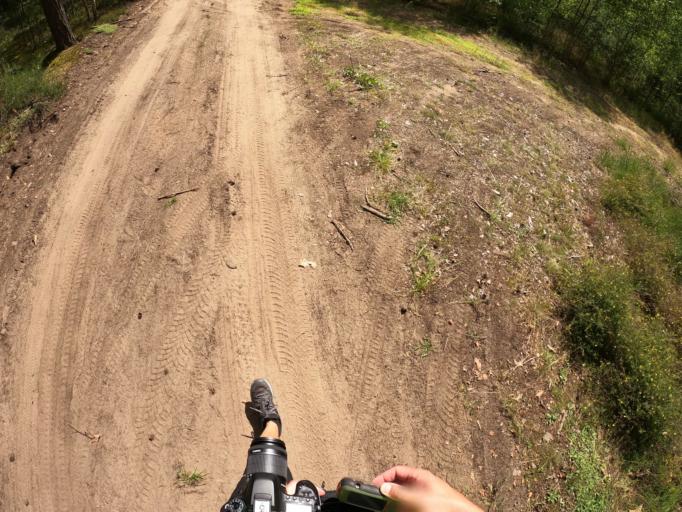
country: LT
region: Alytaus apskritis
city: Druskininkai
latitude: 54.0265
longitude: 23.9232
